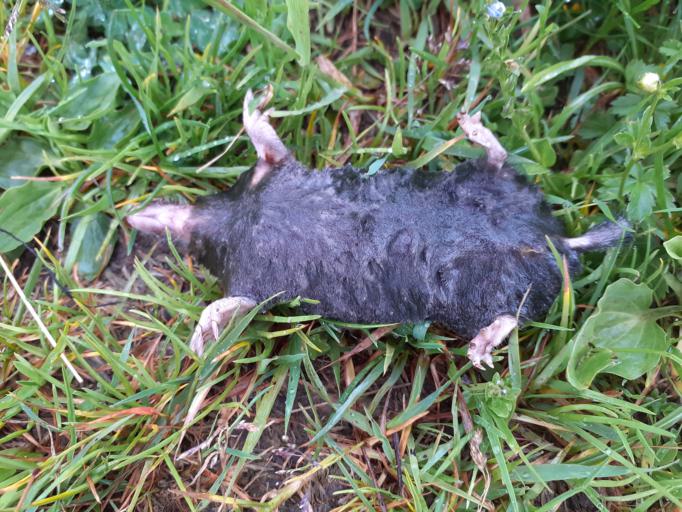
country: IT
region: Piedmont
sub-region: Provincia Verbano-Cusio-Ossola
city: Druogno
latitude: 46.0964
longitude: 8.4419
